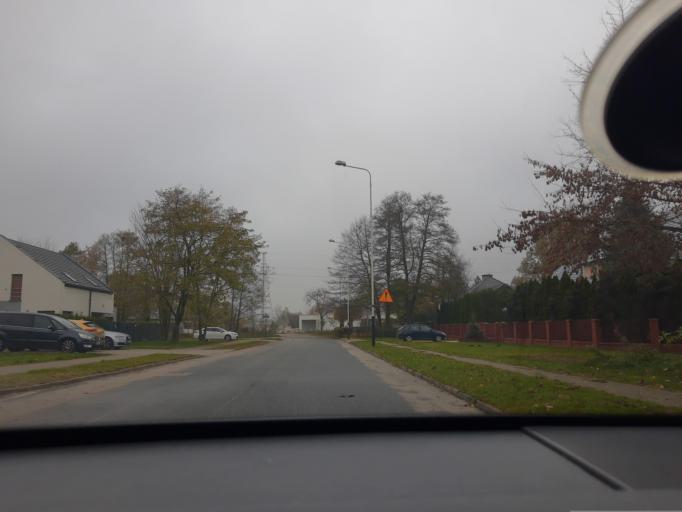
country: PL
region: Lodz Voivodeship
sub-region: Powiat pabianicki
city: Konstantynow Lodzki
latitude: 51.7465
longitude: 19.3770
